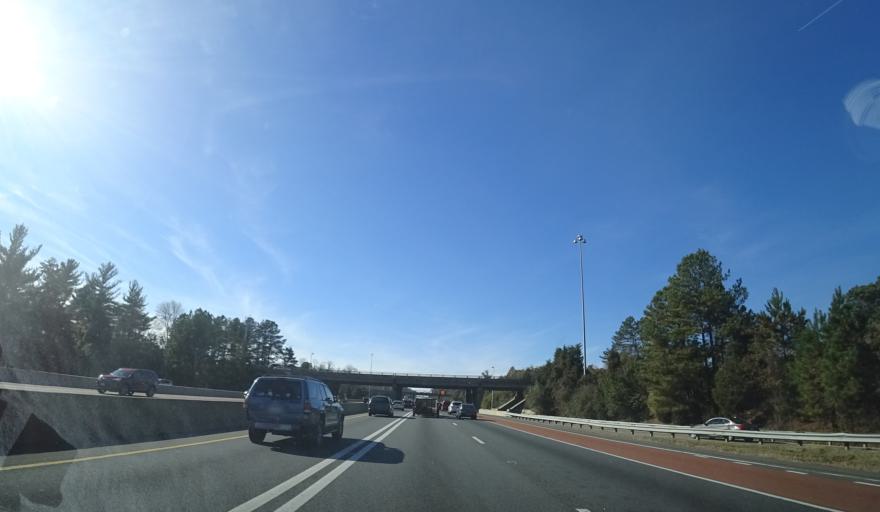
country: US
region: Virginia
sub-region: Fairfax County
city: Oakton
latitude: 38.8694
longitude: -77.3077
